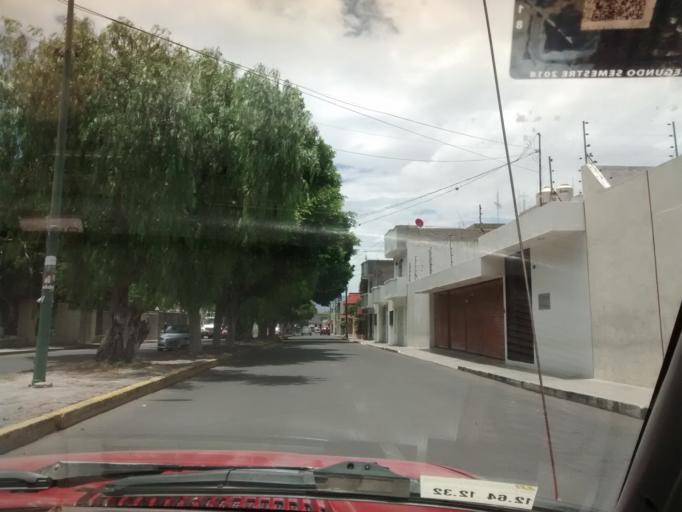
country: MX
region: Puebla
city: Tehuacan
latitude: 18.4623
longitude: -97.4050
